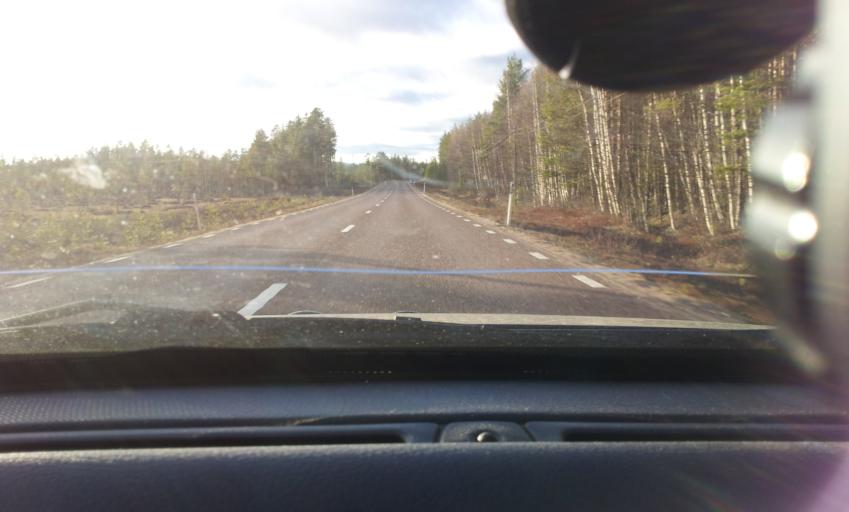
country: SE
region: Jaemtland
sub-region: Harjedalens Kommun
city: Sveg
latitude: 62.1401
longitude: 14.9631
